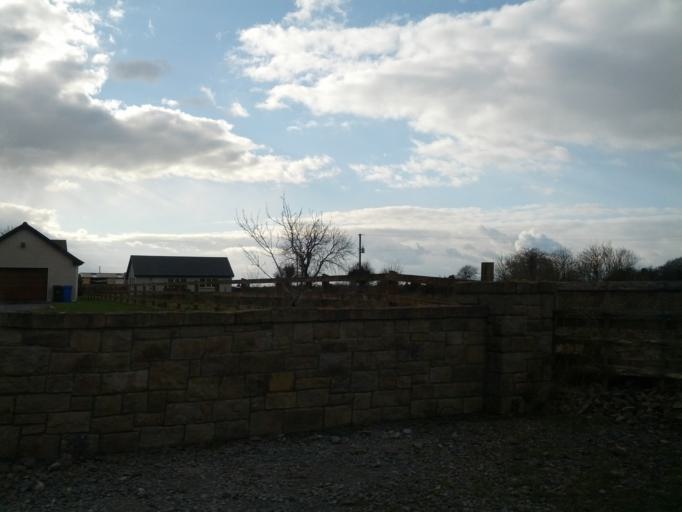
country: IE
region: Connaught
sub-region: County Galway
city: Athenry
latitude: 53.4629
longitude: -8.6486
